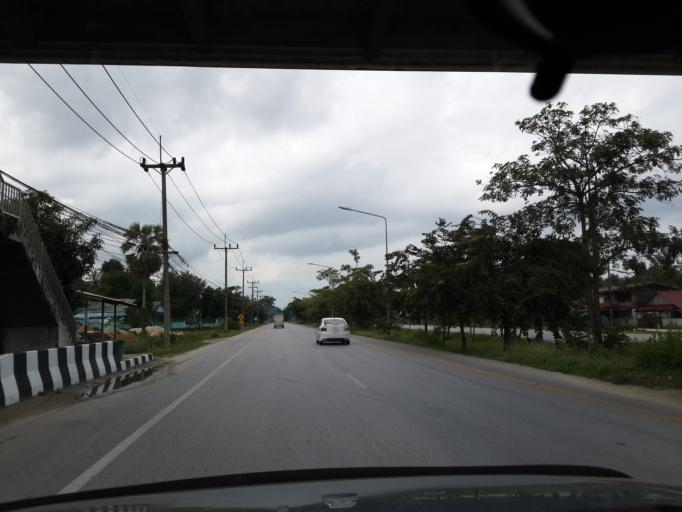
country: TH
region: Pattani
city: Pattani
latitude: 6.8728
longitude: 101.3088
